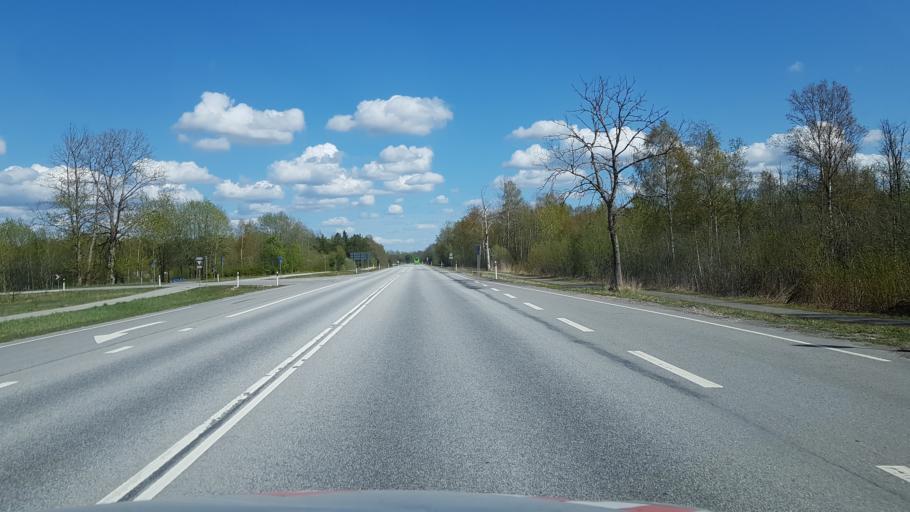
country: EE
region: Laeaene
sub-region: Ridala Parish
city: Uuemoisa
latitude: 58.9492
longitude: 23.6394
